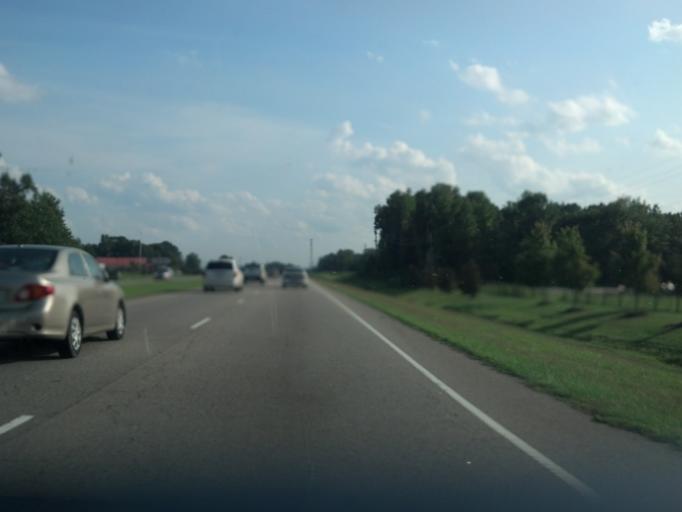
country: US
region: North Carolina
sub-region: Pitt County
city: Winterville
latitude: 35.5347
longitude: -77.4075
